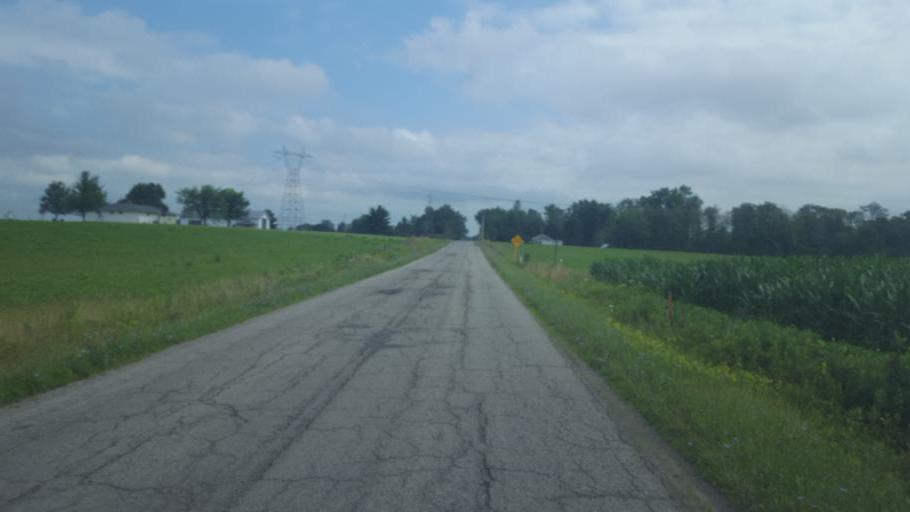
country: US
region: Ohio
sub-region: Crawford County
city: Galion
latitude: 40.6896
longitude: -82.7840
